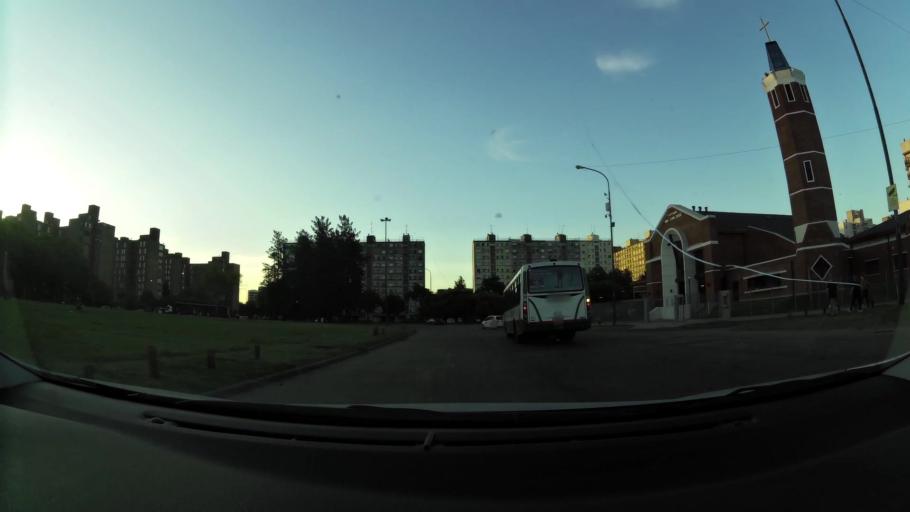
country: AR
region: Buenos Aires F.D.
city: Villa Lugano
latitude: -34.6640
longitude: -58.4691
